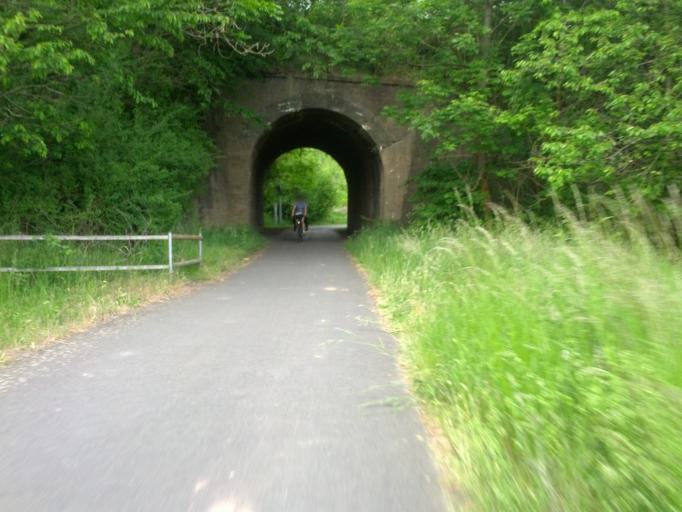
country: DE
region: Thuringia
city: Treffurt
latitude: 51.1346
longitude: 10.2041
